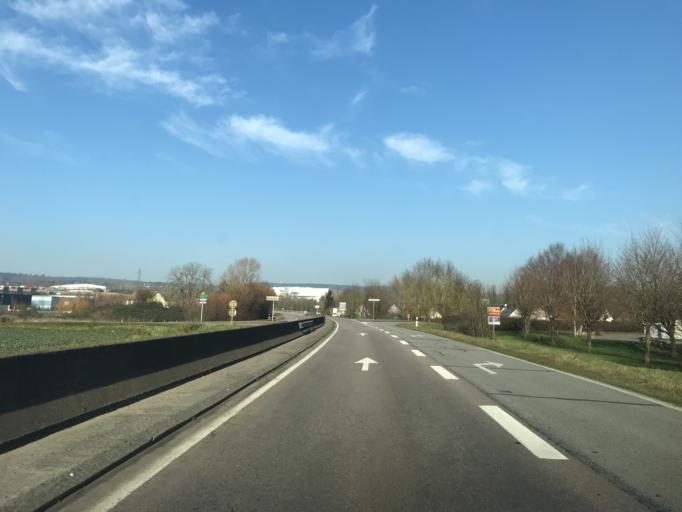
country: FR
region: Haute-Normandie
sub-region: Departement de l'Eure
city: Le Vaudreuil
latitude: 49.2478
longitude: 1.1907
